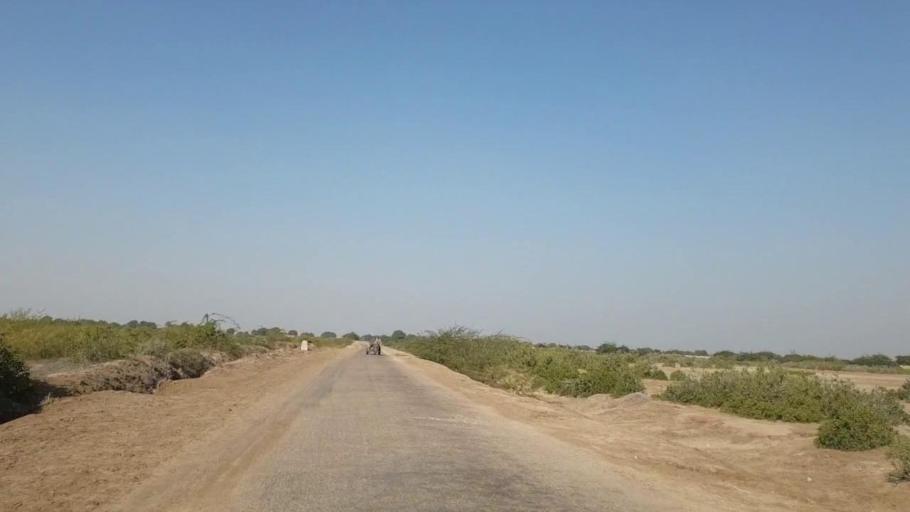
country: PK
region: Sindh
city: Digri
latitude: 25.0002
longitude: 69.1065
